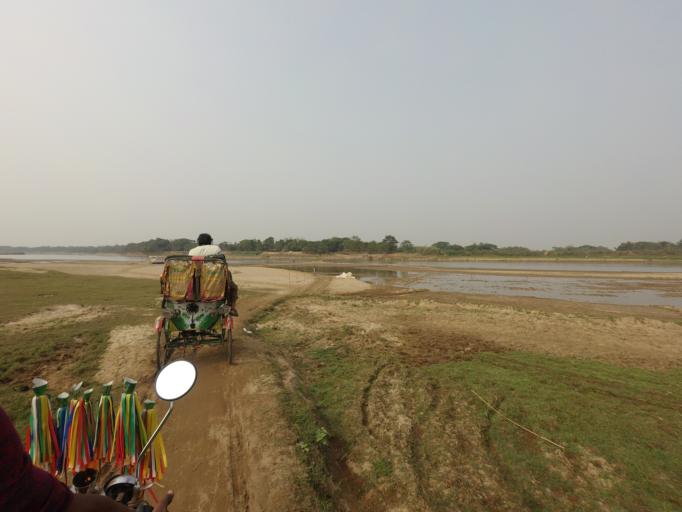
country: BD
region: Dhaka
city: Netrakona
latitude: 25.1024
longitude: 90.6564
